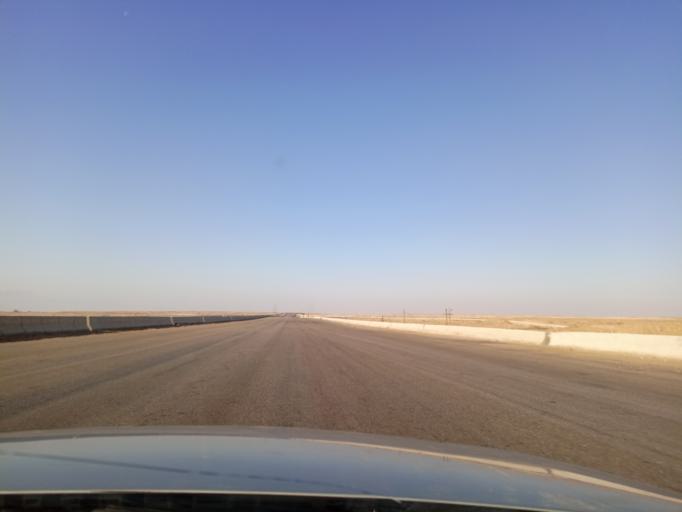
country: EG
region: Muhafazat al Fayyum
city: Tamiyah
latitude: 29.6278
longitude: 30.9630
